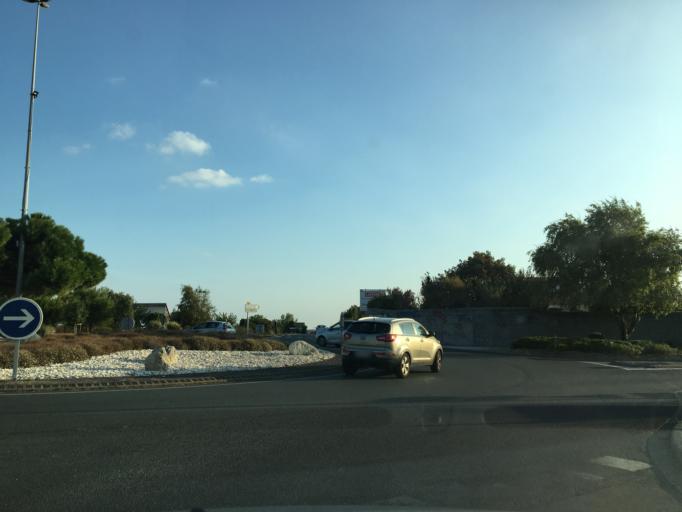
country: FR
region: Poitou-Charentes
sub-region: Departement de la Charente-Maritime
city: Angoulins
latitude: 46.1042
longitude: -1.0980
